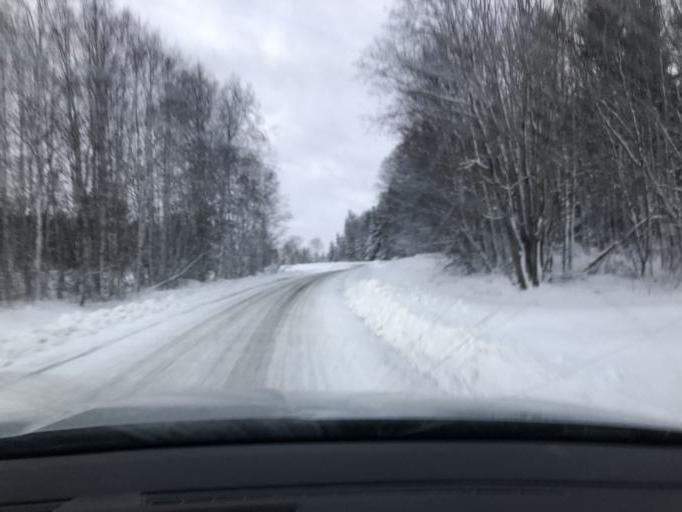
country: SE
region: Vaesternorrland
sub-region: Kramfors Kommun
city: Nordingra
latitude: 62.9156
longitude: 18.2320
